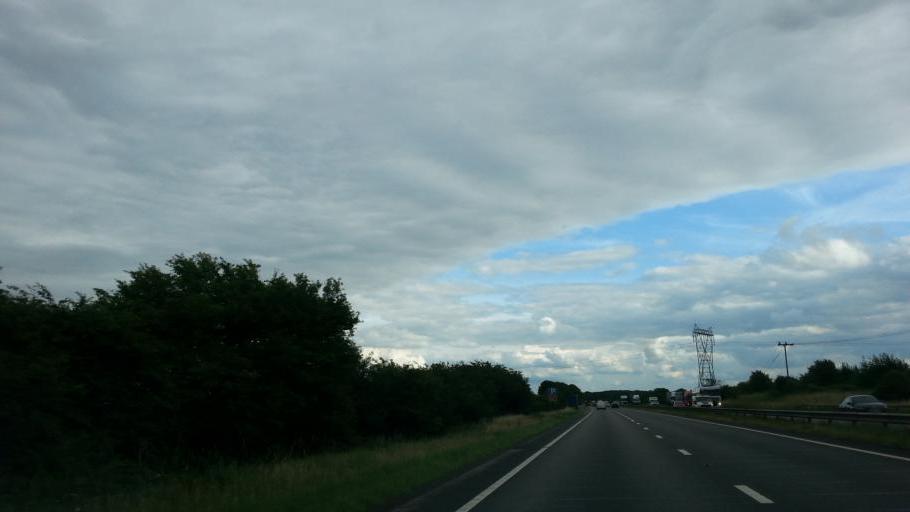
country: GB
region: England
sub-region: Nottinghamshire
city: Tuxford
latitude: 53.2213
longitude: -0.8851
